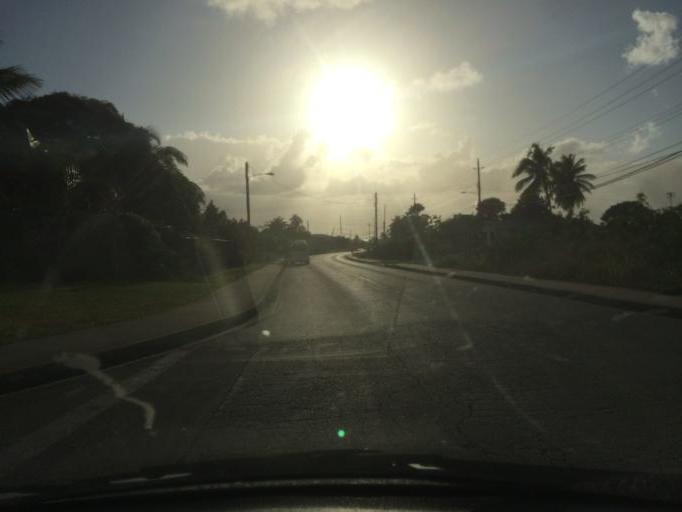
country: BB
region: Saint Lucy
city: Checker Hall
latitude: 13.2863
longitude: -59.6401
